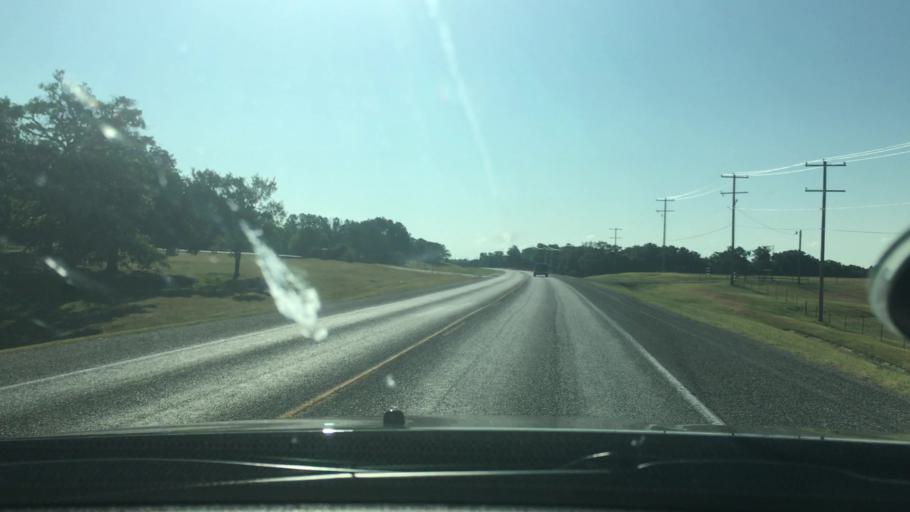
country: US
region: Oklahoma
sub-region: Johnston County
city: Tishomingo
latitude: 34.2374
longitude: -96.7319
